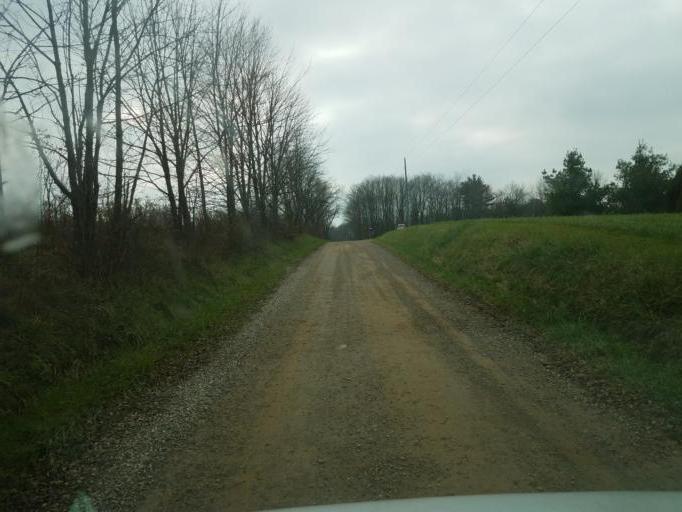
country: US
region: Ohio
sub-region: Knox County
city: Fredericktown
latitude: 40.5174
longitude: -82.4062
